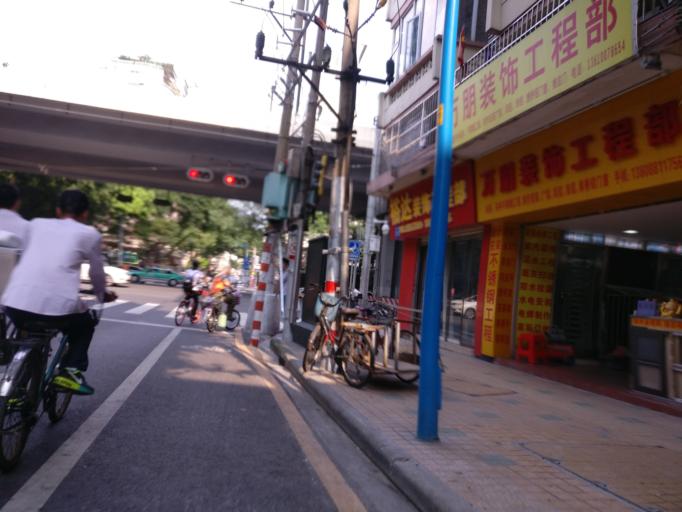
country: CN
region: Guangdong
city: Guangzhou
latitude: 23.1240
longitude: 113.2849
